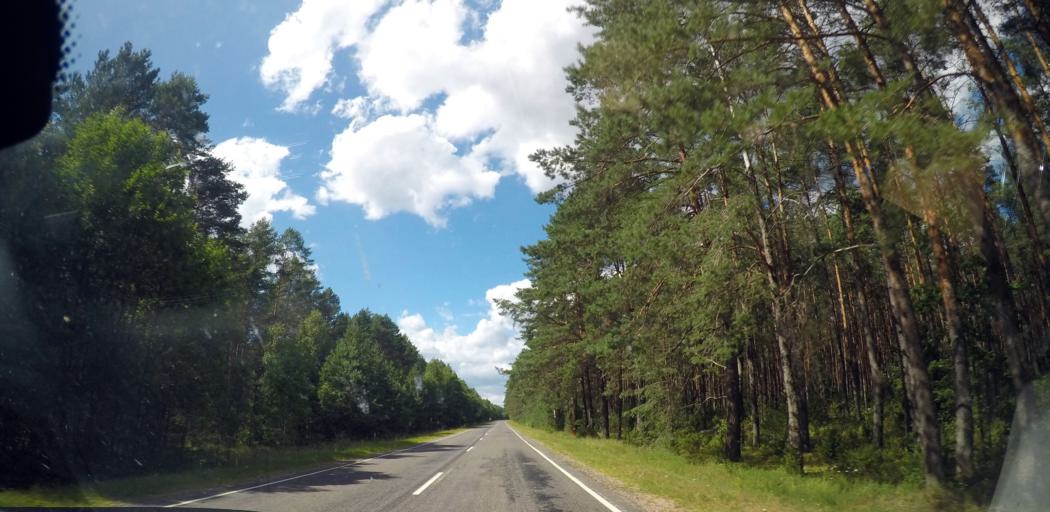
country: BY
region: Grodnenskaya
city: Skidal'
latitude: 53.8492
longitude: 24.1988
